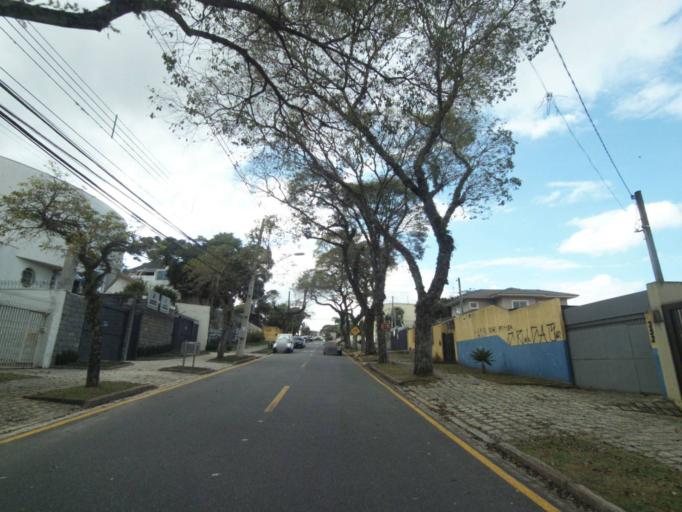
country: BR
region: Parana
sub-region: Curitiba
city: Curitiba
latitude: -25.4203
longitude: -49.2799
